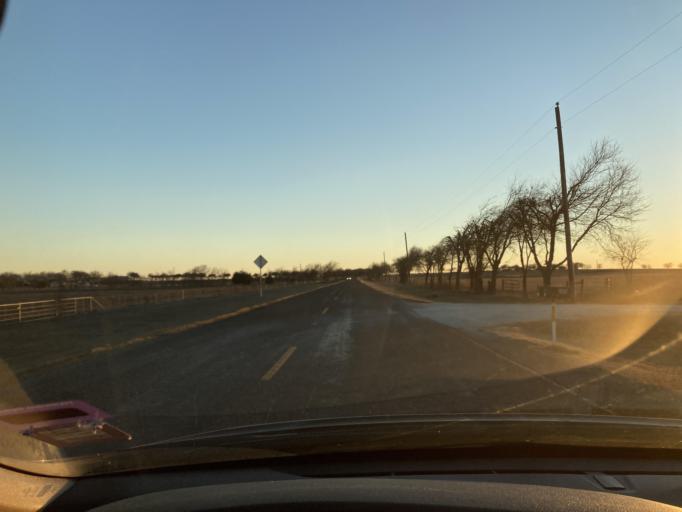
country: US
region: Texas
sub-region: Ellis County
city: Waxahachie
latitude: 32.3117
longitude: -96.8826
